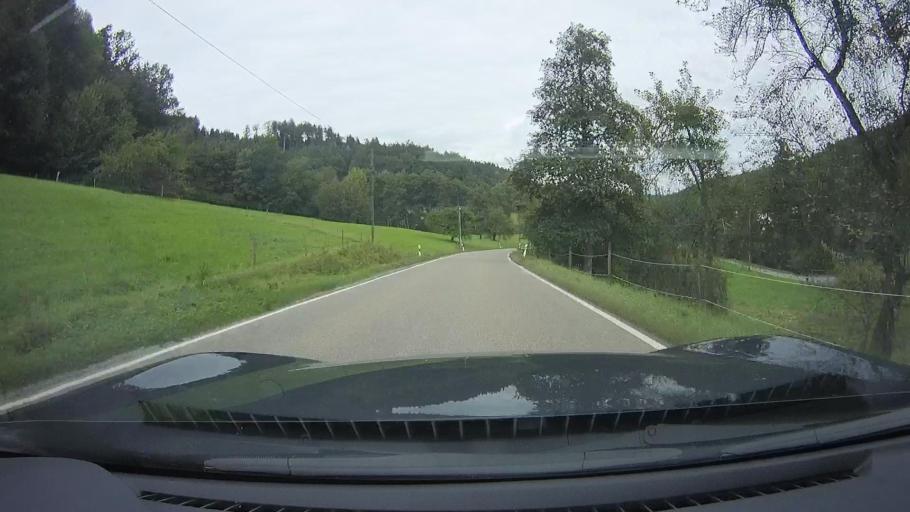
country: DE
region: Baden-Wuerttemberg
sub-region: Regierungsbezirk Stuttgart
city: Kaisersbach
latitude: 48.9544
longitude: 9.6376
